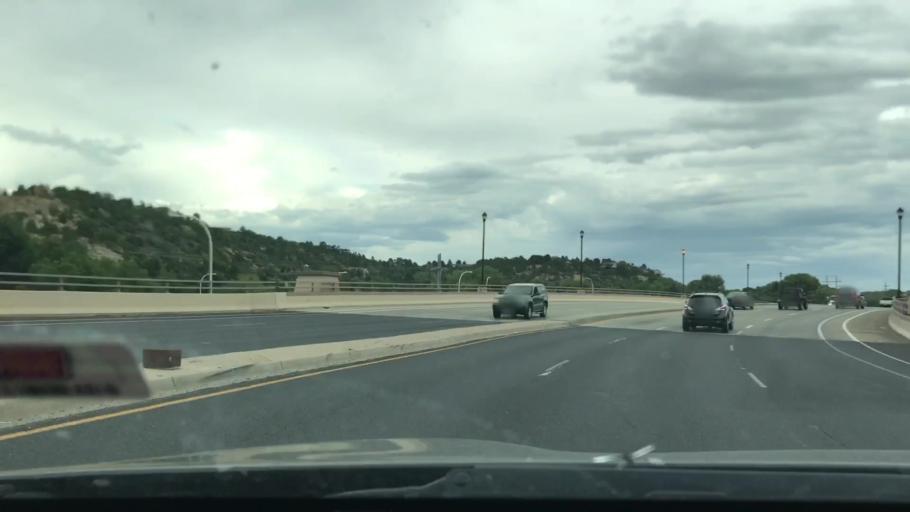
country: US
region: Colorado
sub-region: El Paso County
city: Colorado Springs
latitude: 38.8890
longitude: -104.7868
